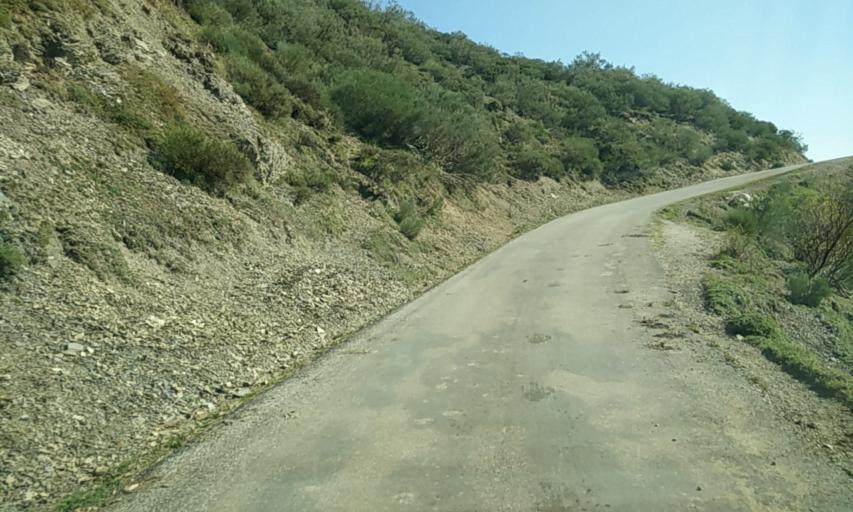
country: ES
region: Cantabria
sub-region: Provincia de Cantabria
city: Camaleno
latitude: 43.0739
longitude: -4.7557
